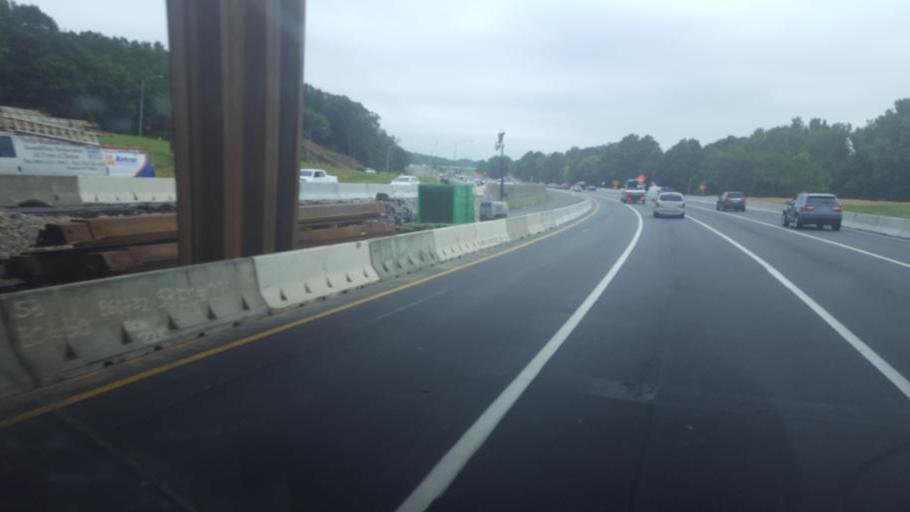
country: US
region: North Carolina
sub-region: Mecklenburg County
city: Charlotte
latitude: 35.2609
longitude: -80.8407
